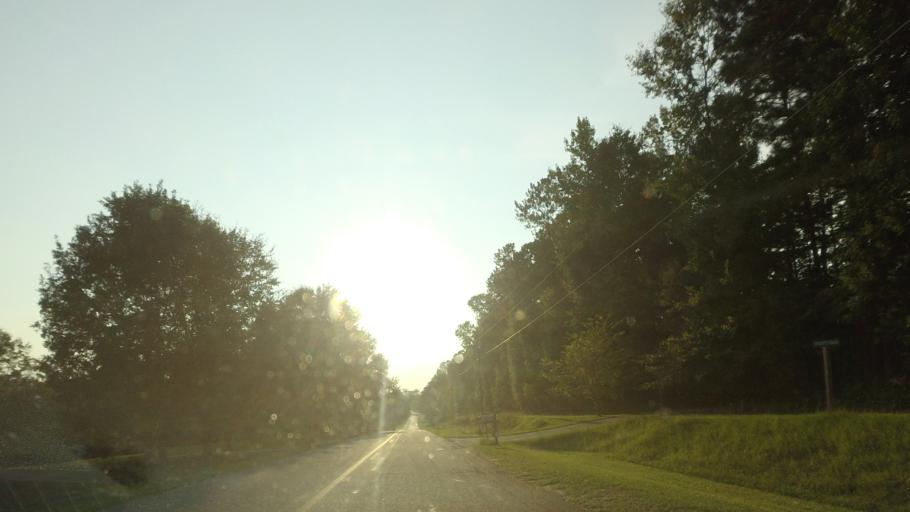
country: US
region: Georgia
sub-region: Bibb County
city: West Point
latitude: 32.9454
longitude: -83.7805
